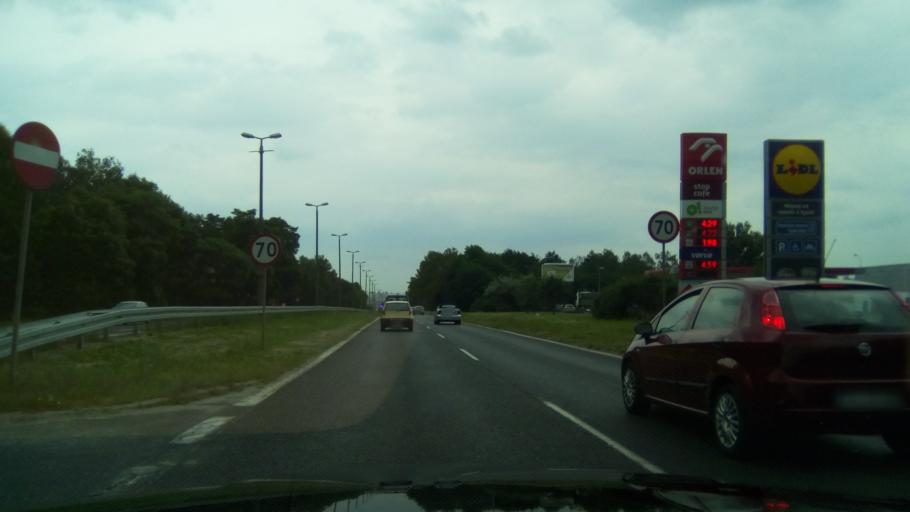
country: PL
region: Greater Poland Voivodeship
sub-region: Powiat poznanski
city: Czerwonak
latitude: 52.4104
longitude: 17.0076
